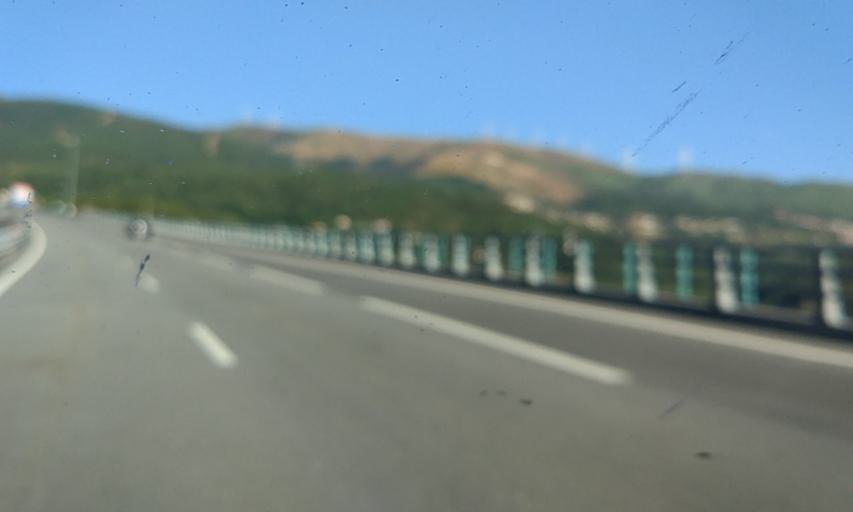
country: PT
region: Porto
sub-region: Baiao
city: Valadares
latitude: 41.2528
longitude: -7.9674
